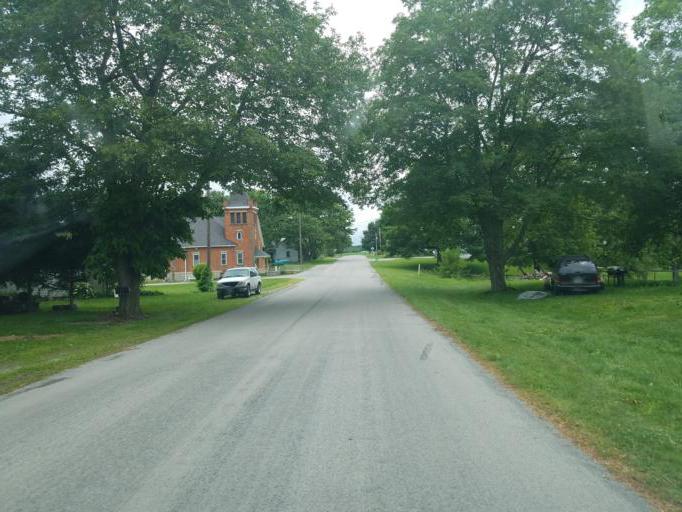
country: US
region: Ohio
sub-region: Wyandot County
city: Upper Sandusky
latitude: 40.7395
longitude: -83.2157
